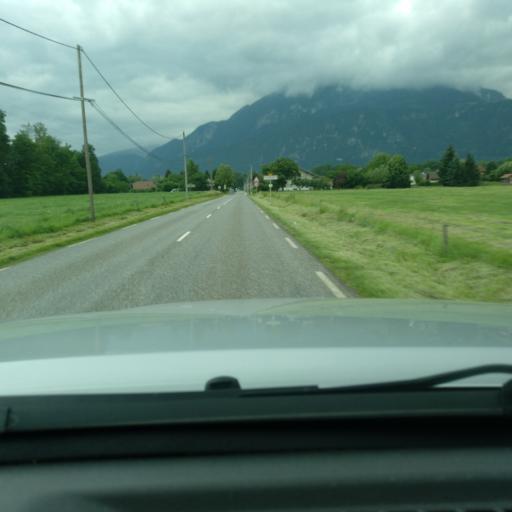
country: FR
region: Rhone-Alpes
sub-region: Departement de la Haute-Savoie
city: Amancy
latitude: 46.0850
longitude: 6.3613
